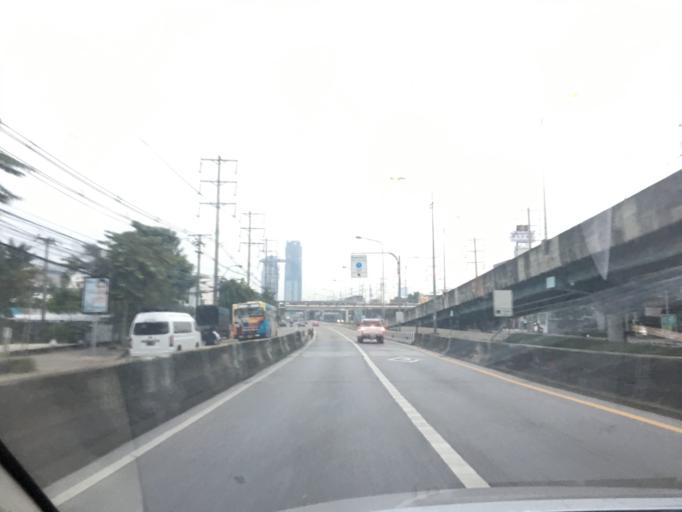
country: TH
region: Bangkok
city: Yan Nawa
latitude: 13.6805
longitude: 100.5275
